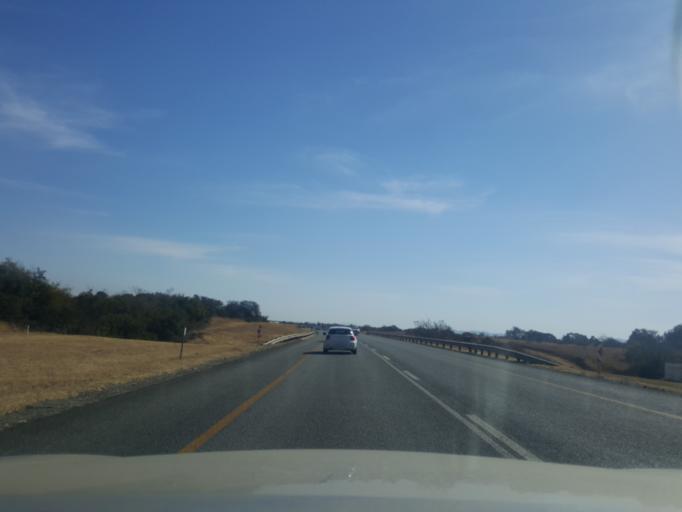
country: ZA
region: North-West
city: Ga-Rankuwa
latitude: -25.6504
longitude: 27.9664
